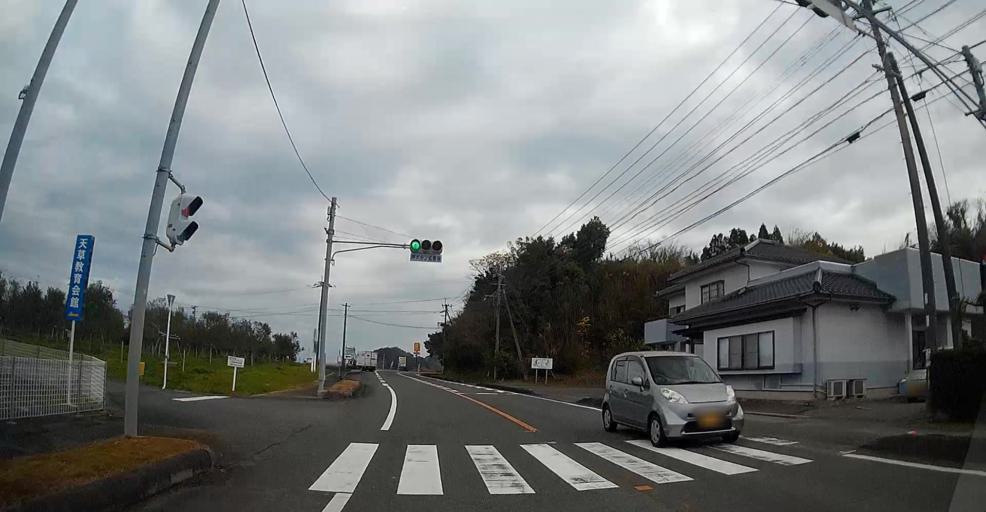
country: JP
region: Kumamoto
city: Hondo
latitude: 32.4604
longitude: 130.2301
